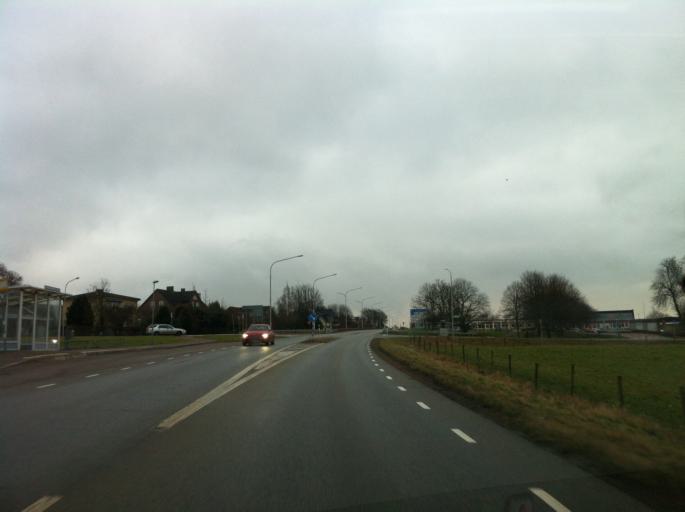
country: SE
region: Skane
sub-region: Helsingborg
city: Glumslov
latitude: 55.9446
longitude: 12.8070
